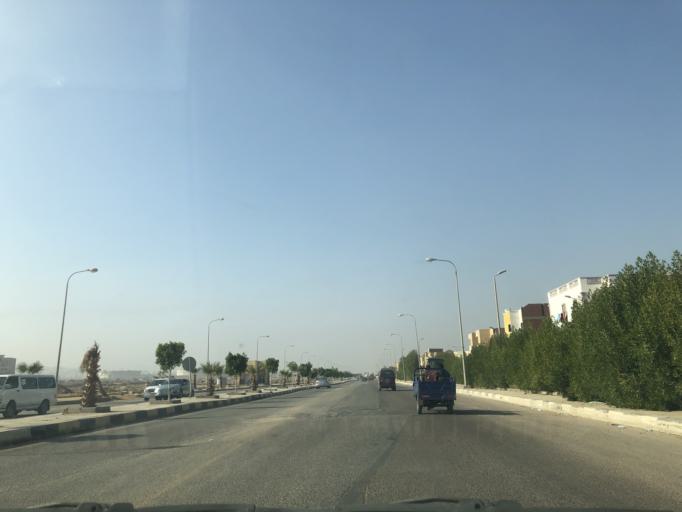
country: EG
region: Al Jizah
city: Madinat Sittah Uktubar
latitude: 29.9285
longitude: 31.0496
